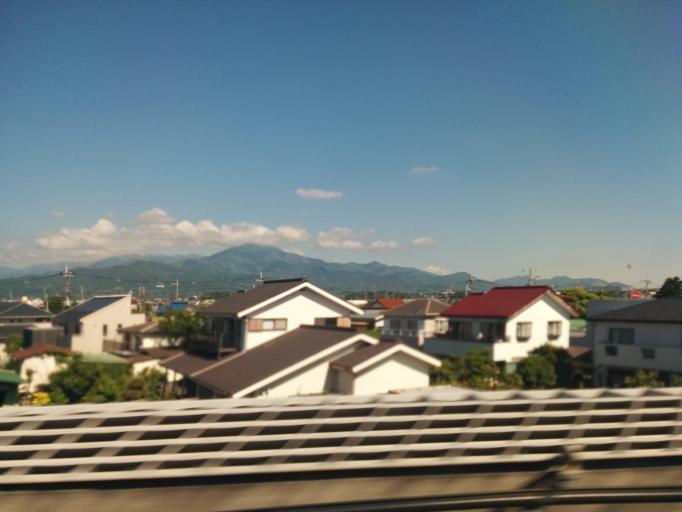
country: JP
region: Kanagawa
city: Isehara
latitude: 35.3593
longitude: 139.3254
